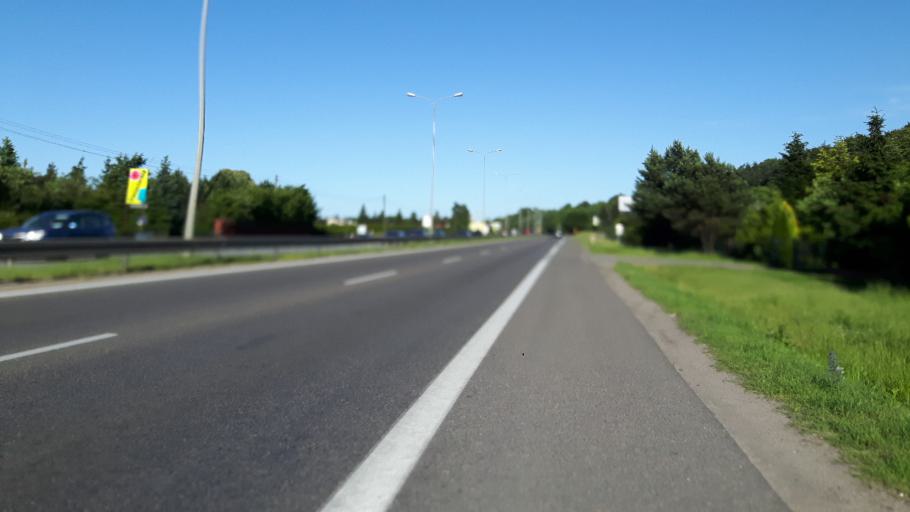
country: PL
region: Pomeranian Voivodeship
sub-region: Powiat wejherowski
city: Reda
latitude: 54.6045
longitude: 18.3215
